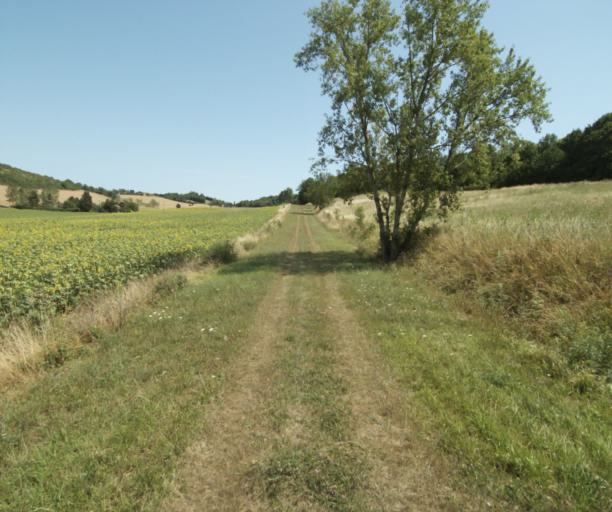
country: FR
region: Midi-Pyrenees
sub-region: Departement de la Haute-Garonne
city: Saint-Felix-Lauragais
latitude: 43.4544
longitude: 1.8784
